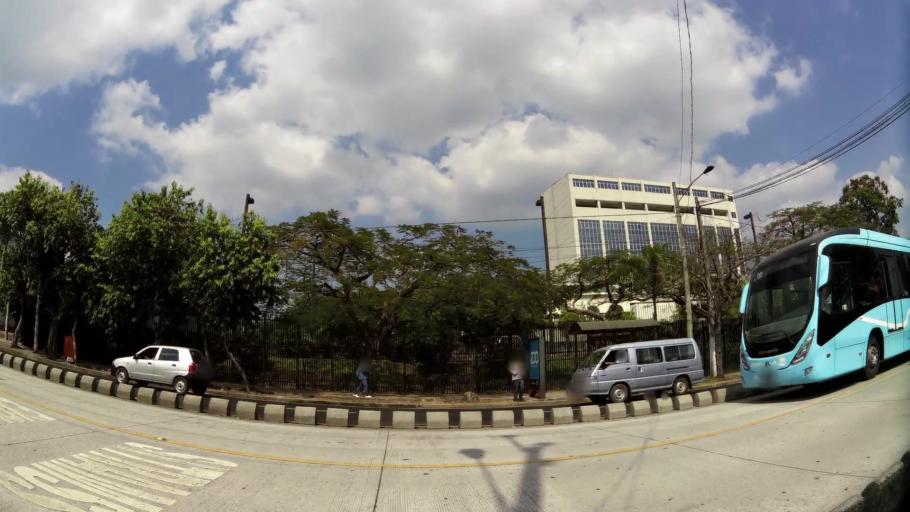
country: SV
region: San Salvador
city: San Salvador
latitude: 13.7033
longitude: -89.1994
